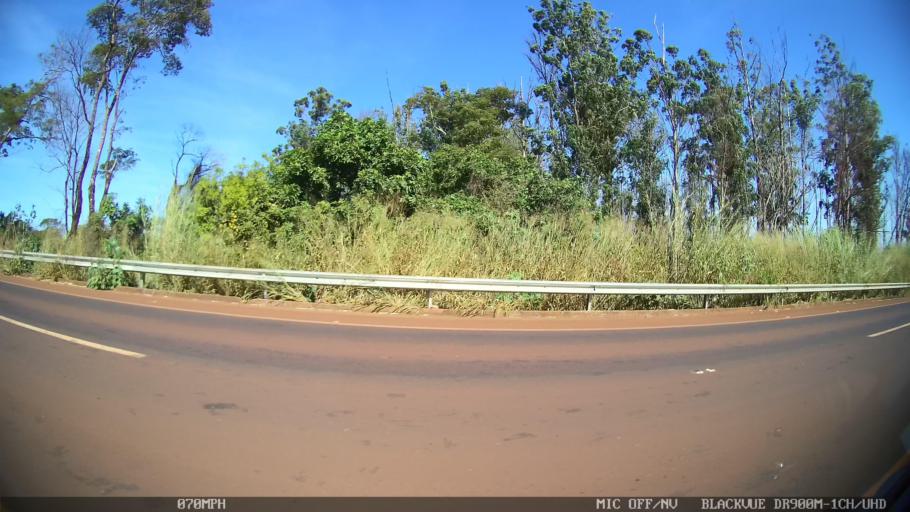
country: BR
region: Sao Paulo
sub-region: Sao Joaquim Da Barra
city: Sao Joaquim da Barra
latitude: -20.5484
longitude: -47.7590
